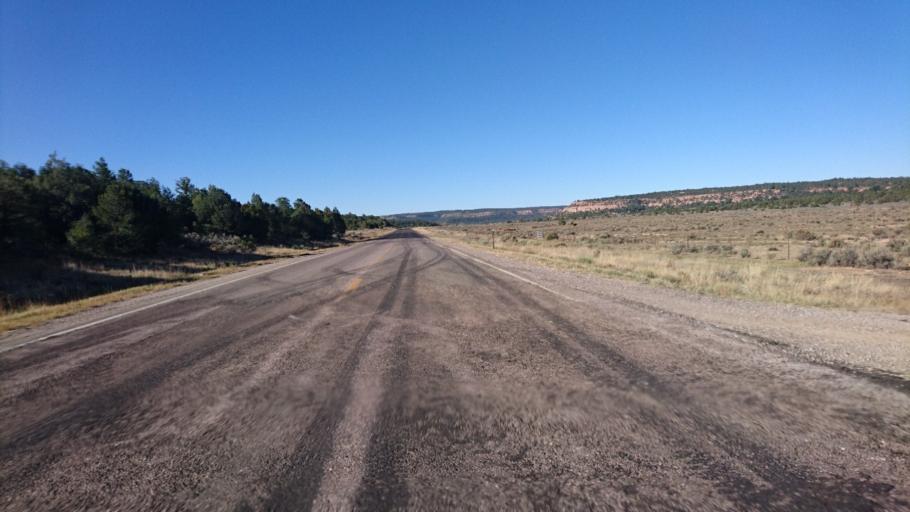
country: US
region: New Mexico
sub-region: McKinley County
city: Black Rock
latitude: 35.1185
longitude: -108.5476
